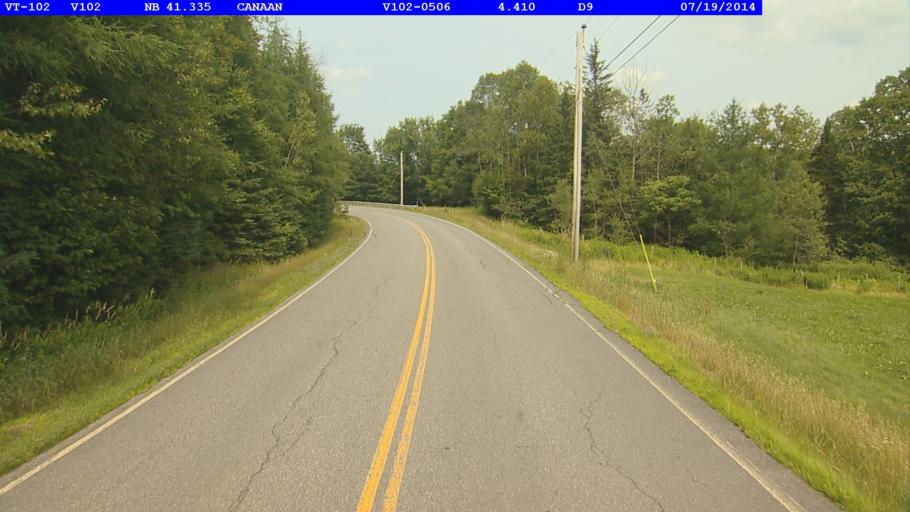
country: US
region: New Hampshire
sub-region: Coos County
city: Colebrook
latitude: 44.9681
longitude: -71.5256
